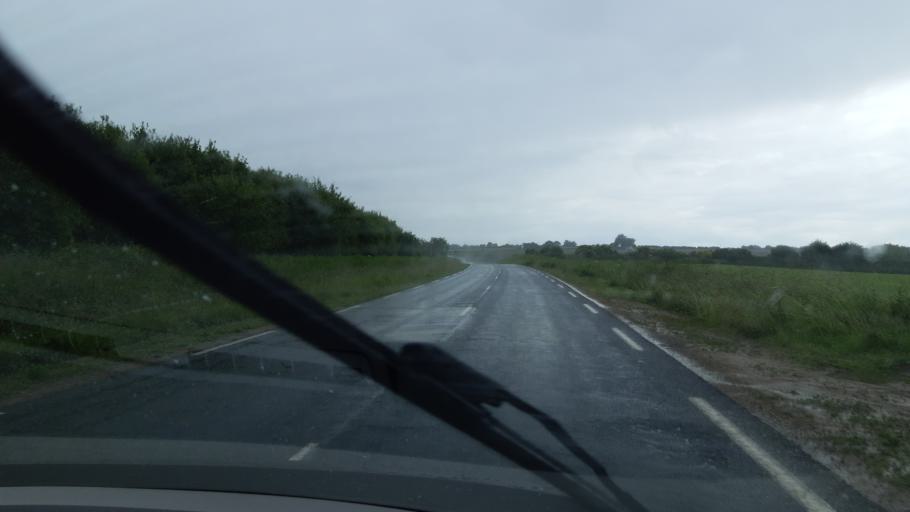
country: FR
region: Brittany
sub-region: Departement du Finistere
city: Plouvorn
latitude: 48.6134
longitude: -4.0566
